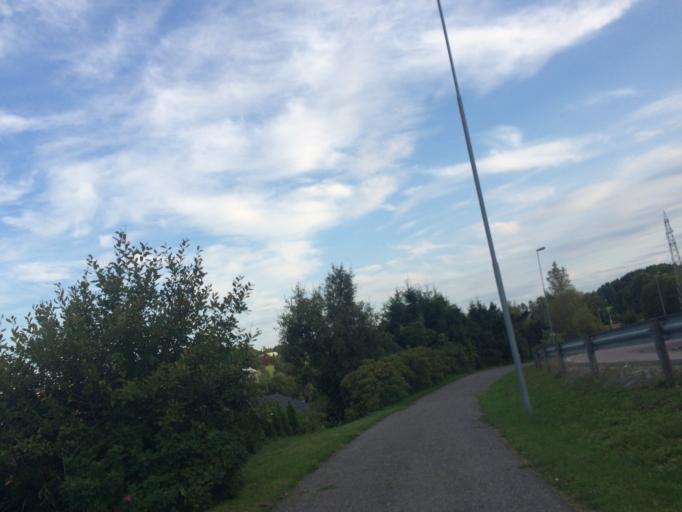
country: NO
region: Akershus
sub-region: Ski
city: Ski
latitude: 59.6748
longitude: 10.8868
